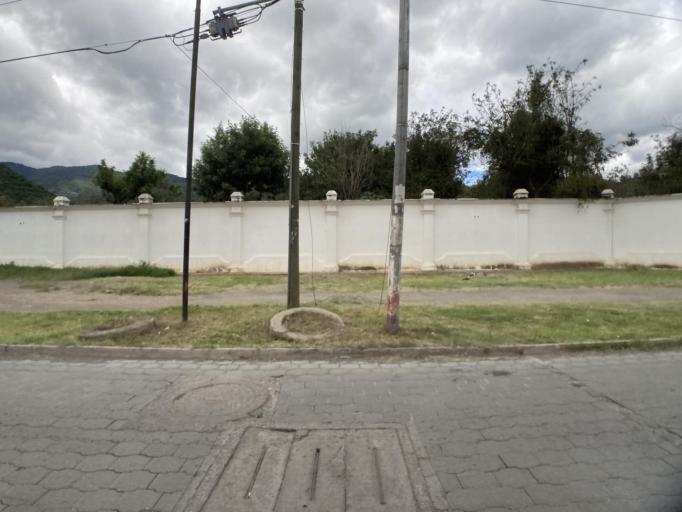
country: GT
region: Sacatepequez
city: Jocotenango
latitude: 14.5759
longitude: -90.7372
